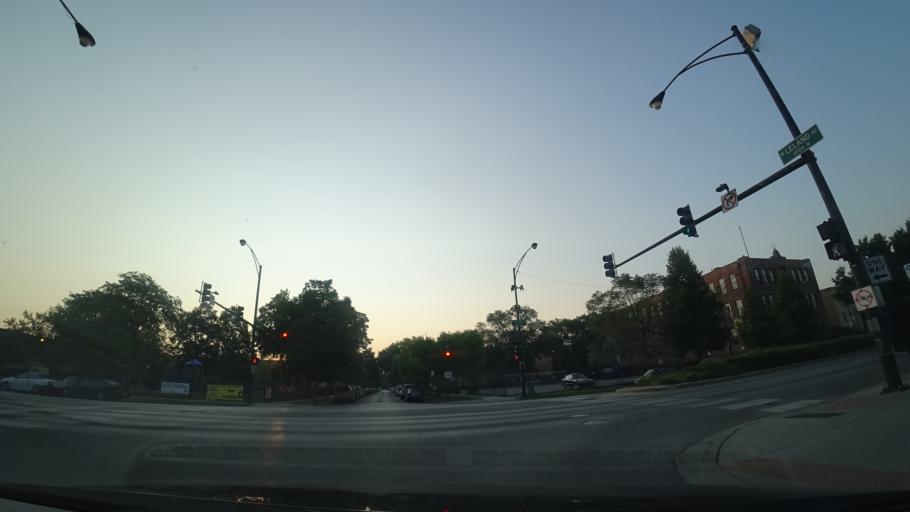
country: US
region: Illinois
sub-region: Cook County
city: Lincolnwood
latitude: 41.9670
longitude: -87.6696
